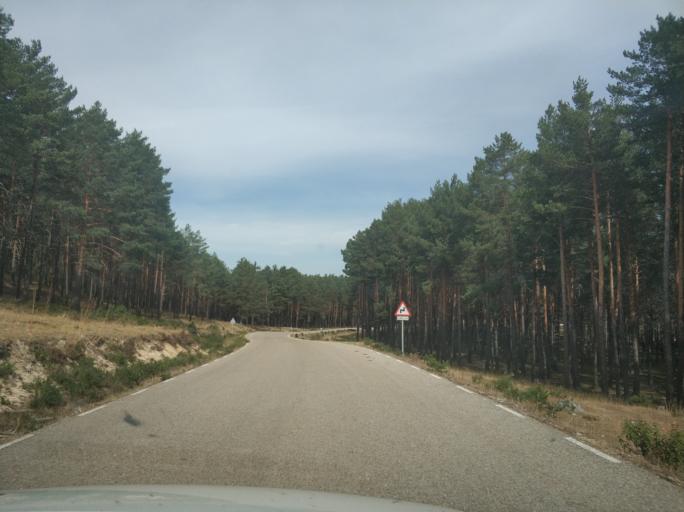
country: ES
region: Castille and Leon
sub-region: Provincia de Soria
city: Navaleno
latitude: 41.8633
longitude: -2.9411
